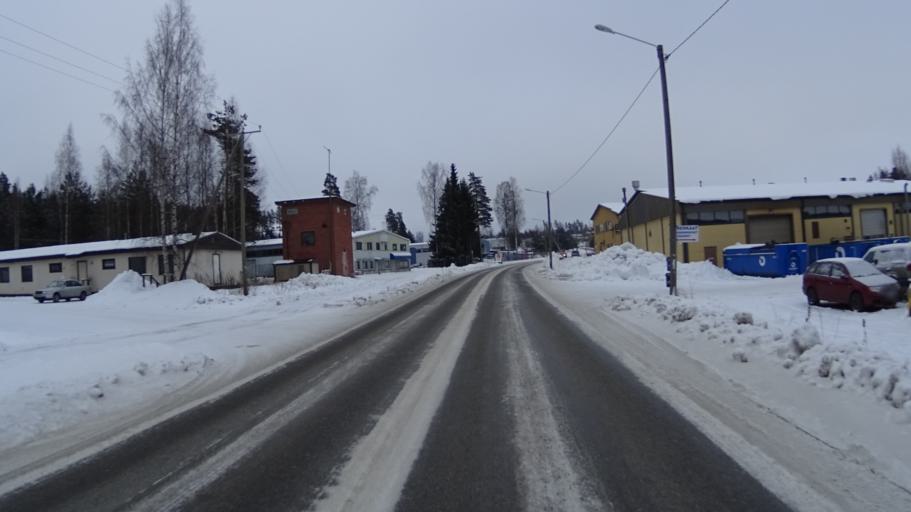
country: FI
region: Uusimaa
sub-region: Helsinki
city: Karkkila
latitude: 60.5219
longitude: 24.2373
